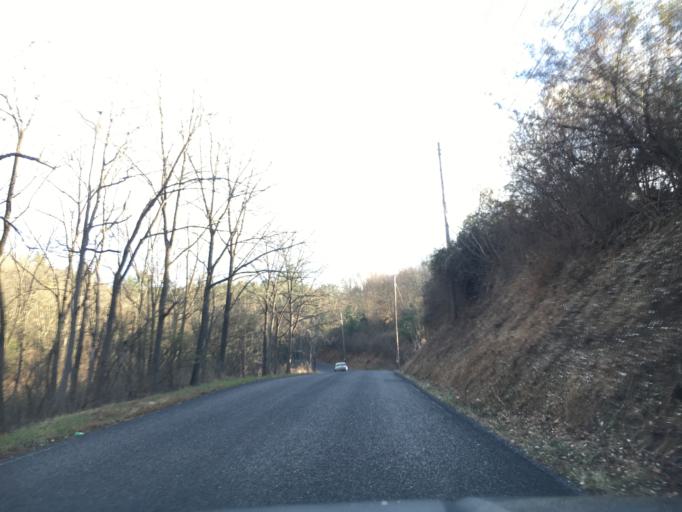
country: US
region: Pennsylvania
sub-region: Carbon County
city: Lehighton
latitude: 40.8090
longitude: -75.7432
